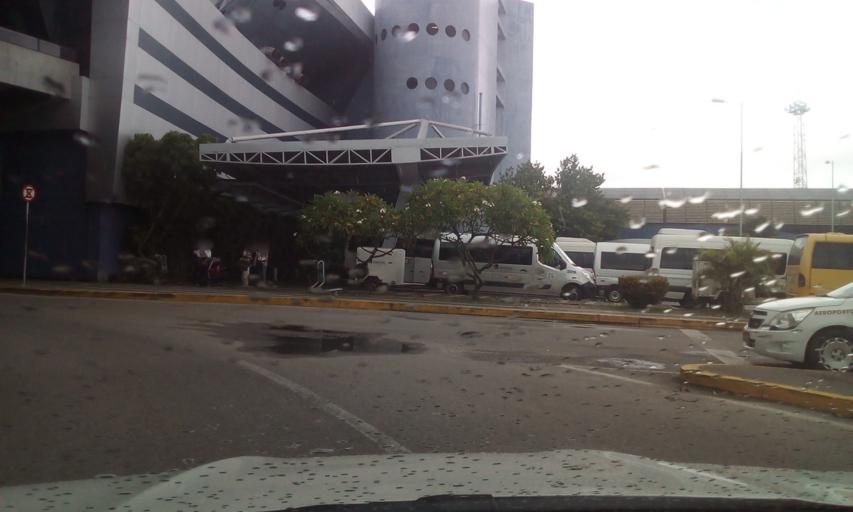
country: BR
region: Pernambuco
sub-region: Recife
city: Recife
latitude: -8.1302
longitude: -34.9182
